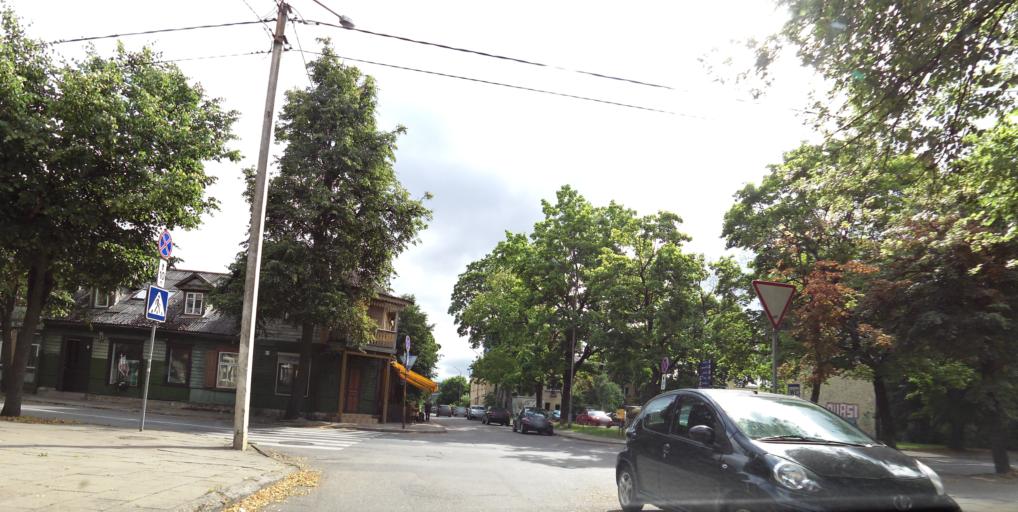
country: LT
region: Vilnius County
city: Naujamiestis
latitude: 54.6921
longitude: 25.2559
